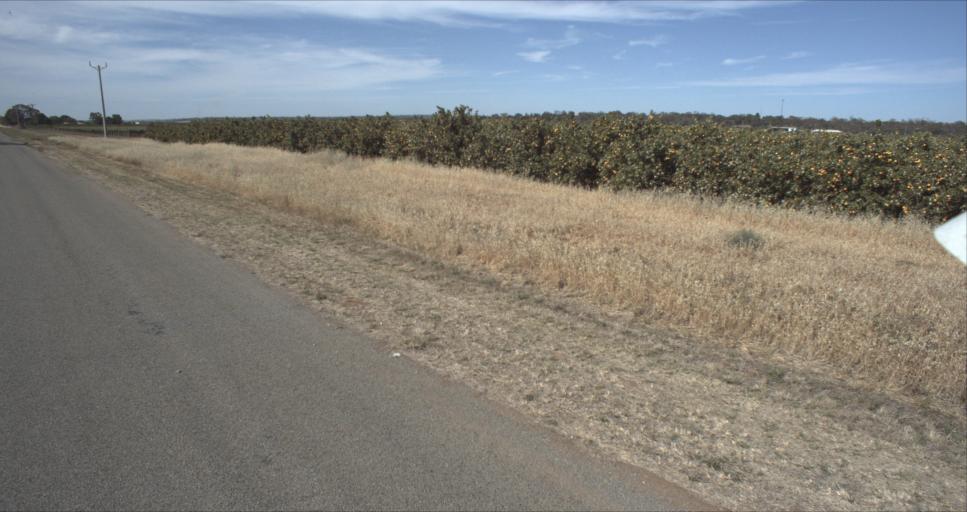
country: AU
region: New South Wales
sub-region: Leeton
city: Leeton
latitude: -34.5592
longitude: 146.4678
